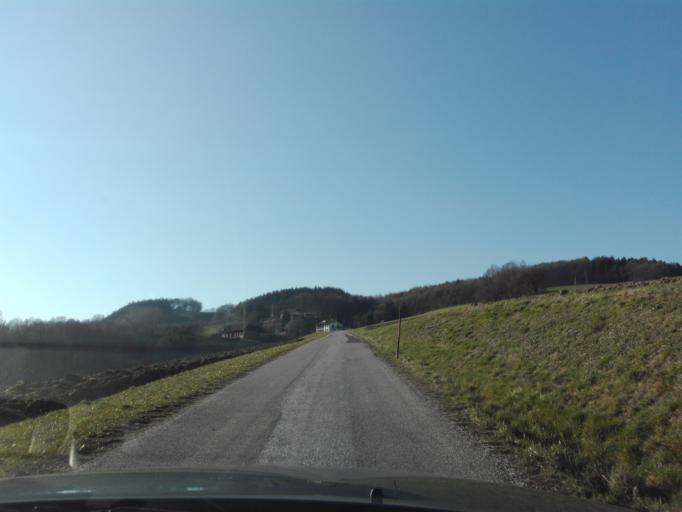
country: AT
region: Upper Austria
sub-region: Politischer Bezirk Rohrbach
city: Kleinzell im Muehlkreis
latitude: 48.3789
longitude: 13.9654
